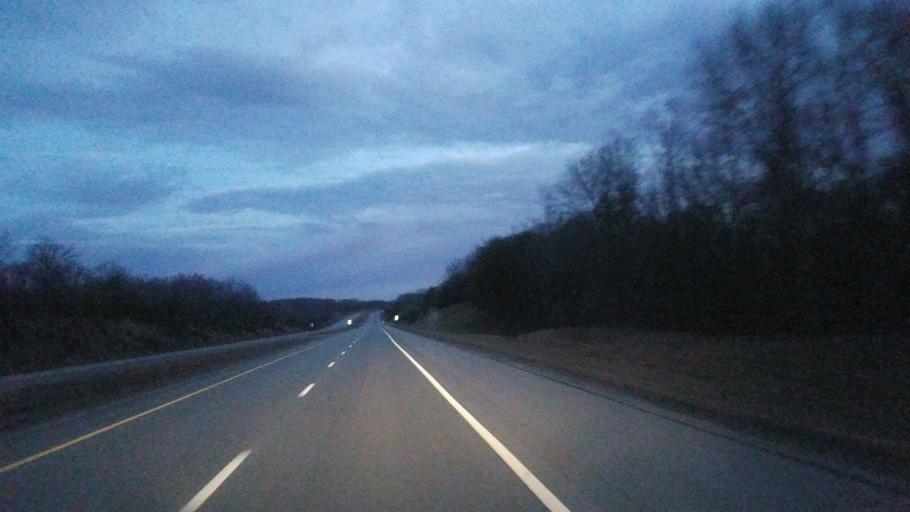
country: US
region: Tennessee
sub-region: Van Buren County
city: Spencer
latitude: 35.5722
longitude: -85.4716
